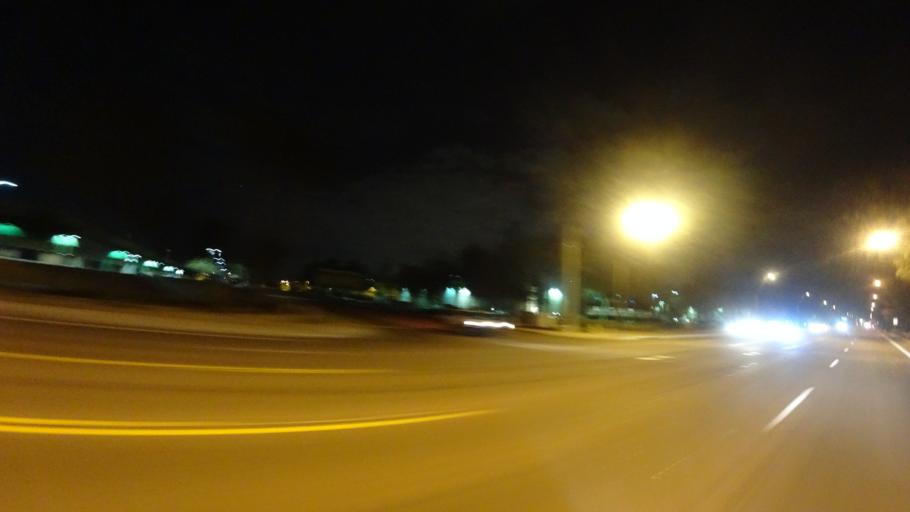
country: US
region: Arizona
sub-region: Maricopa County
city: Guadalupe
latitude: 33.3417
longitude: -111.9457
